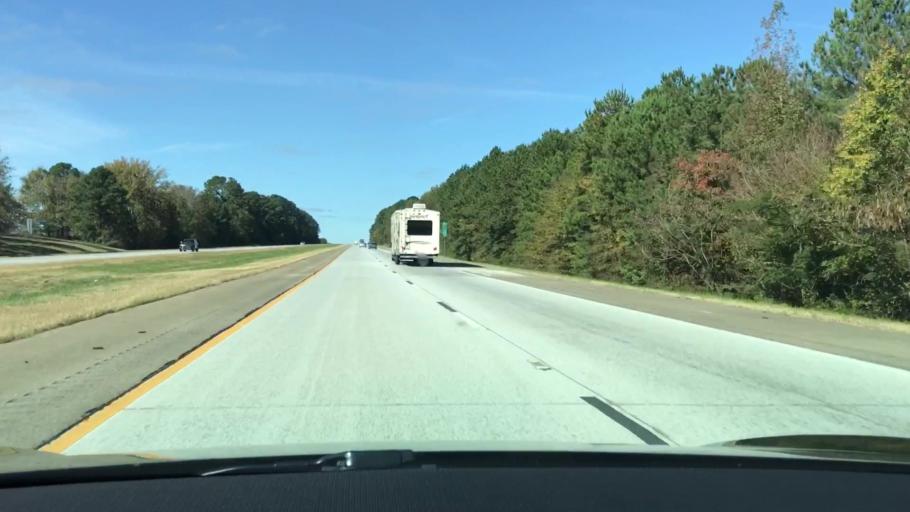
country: US
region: Georgia
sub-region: Putnam County
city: Jefferson
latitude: 33.5362
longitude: -83.3028
